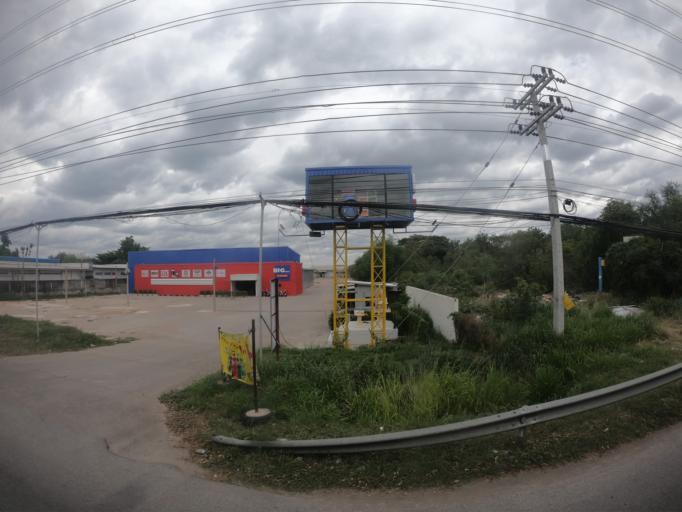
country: TH
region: Nakhon Ratchasima
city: Nakhon Ratchasima
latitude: 14.9389
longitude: 102.1326
